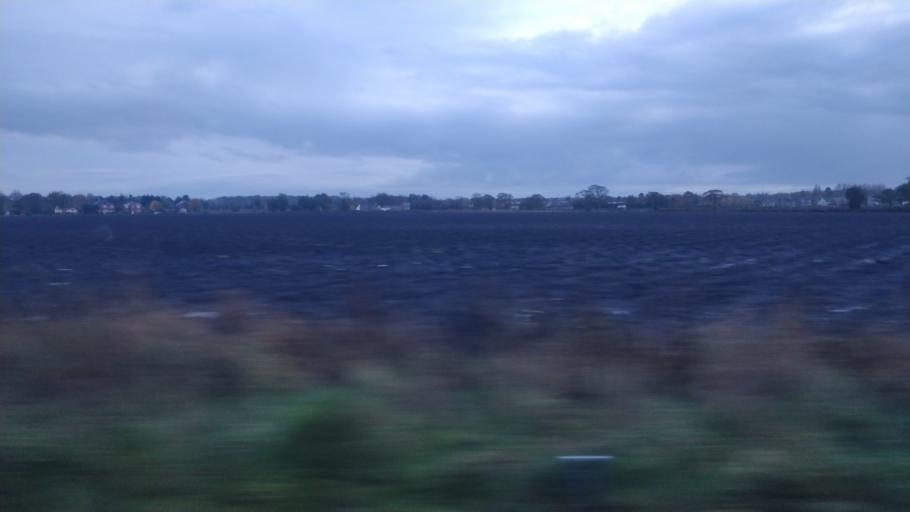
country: GB
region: England
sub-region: Lancashire
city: Parbold
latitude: 53.5993
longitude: -2.8111
